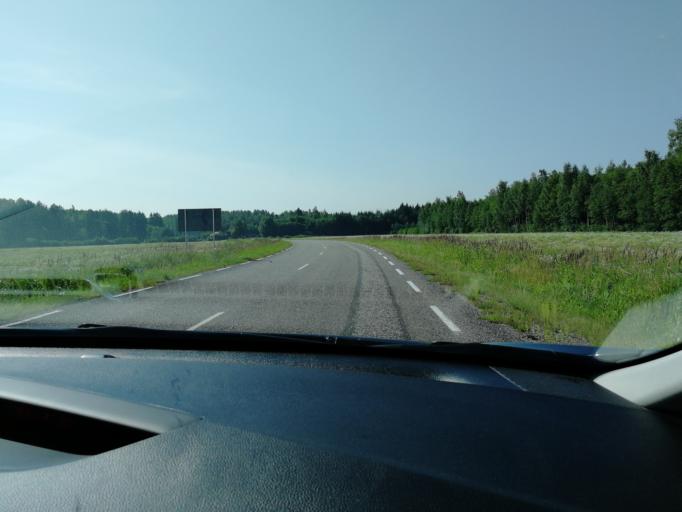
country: EE
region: Paernumaa
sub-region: Saarde vald
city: Kilingi-Nomme
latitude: 58.0181
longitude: 25.0074
